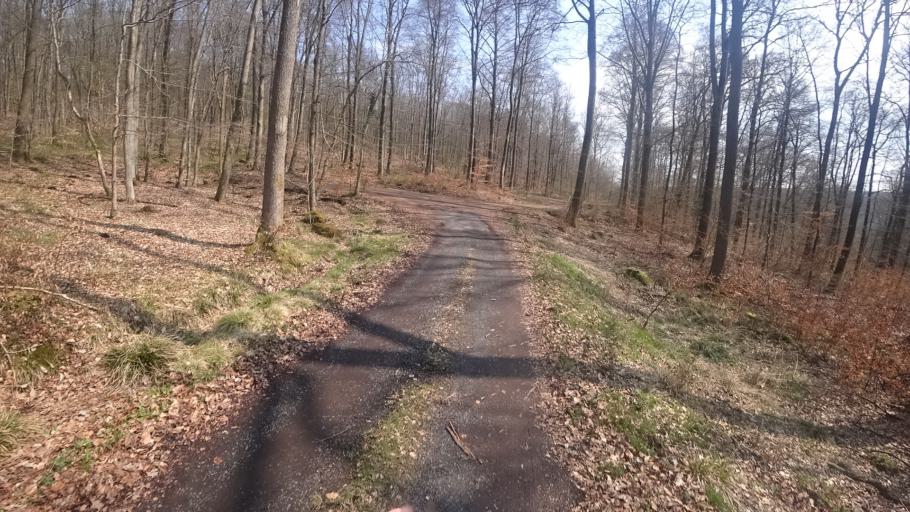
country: DE
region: Rheinland-Pfalz
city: Nauroth
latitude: 50.6896
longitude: 7.8639
